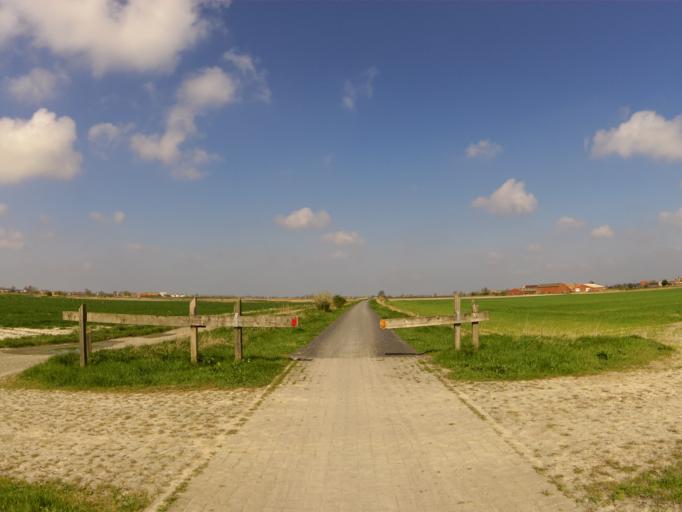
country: BE
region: Flanders
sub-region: Provincie West-Vlaanderen
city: Diksmuide
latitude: 51.0438
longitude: 2.8287
